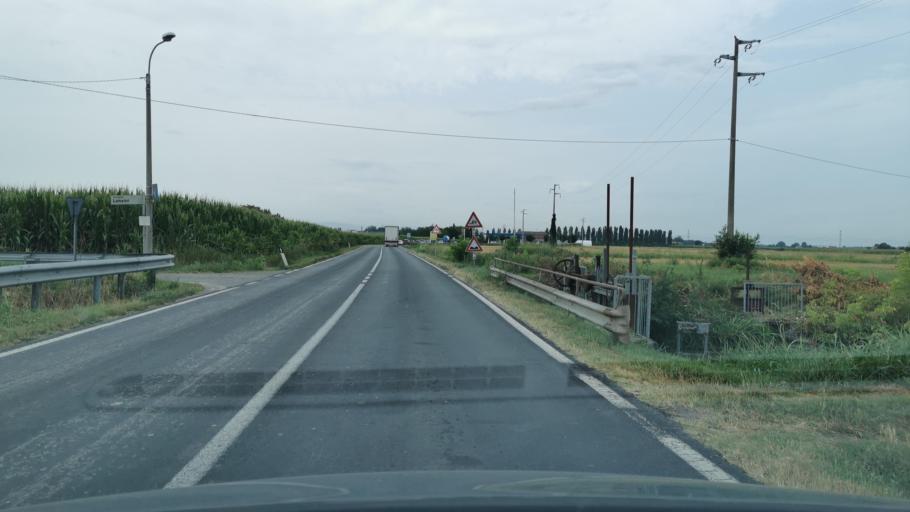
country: IT
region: Emilia-Romagna
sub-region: Provincia di Modena
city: Villanova
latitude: 44.7055
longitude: 10.8977
